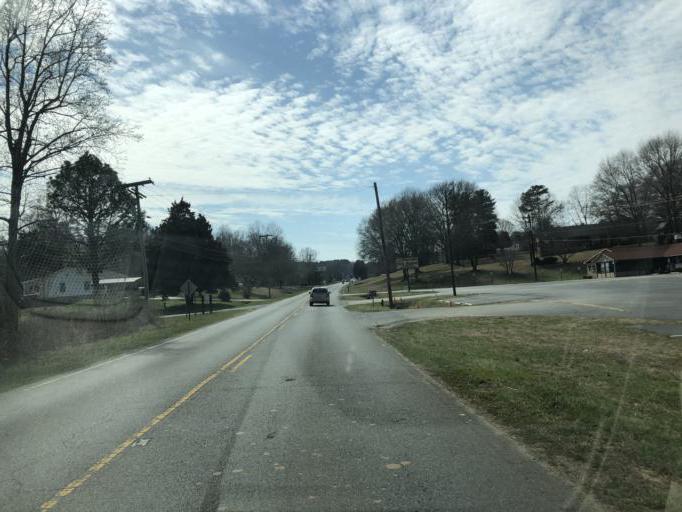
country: US
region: North Carolina
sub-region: Gaston County
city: Ranlo
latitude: 35.3298
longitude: -81.1335
